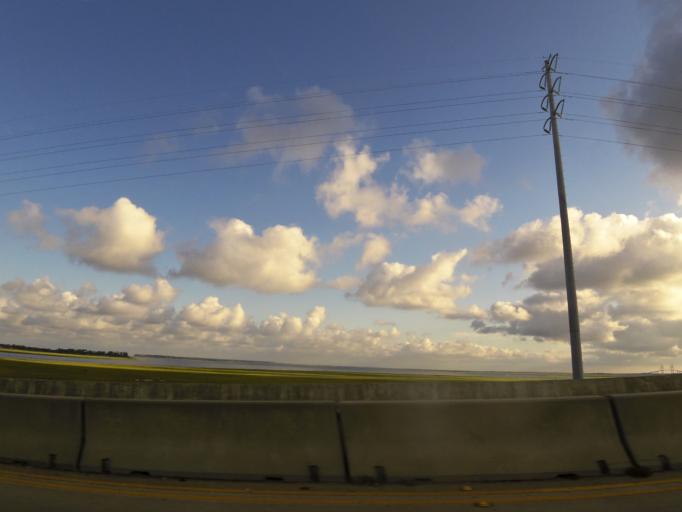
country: US
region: Georgia
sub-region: Glynn County
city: Saint Simon Mills
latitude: 31.1709
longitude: -81.4229
